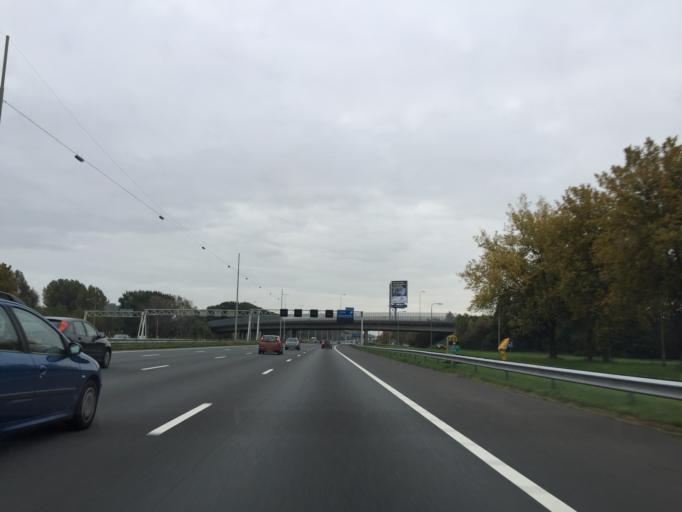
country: NL
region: South Holland
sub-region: Gemeente Zwijndrecht
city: Zwijndrecht
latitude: 51.8332
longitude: 4.6201
